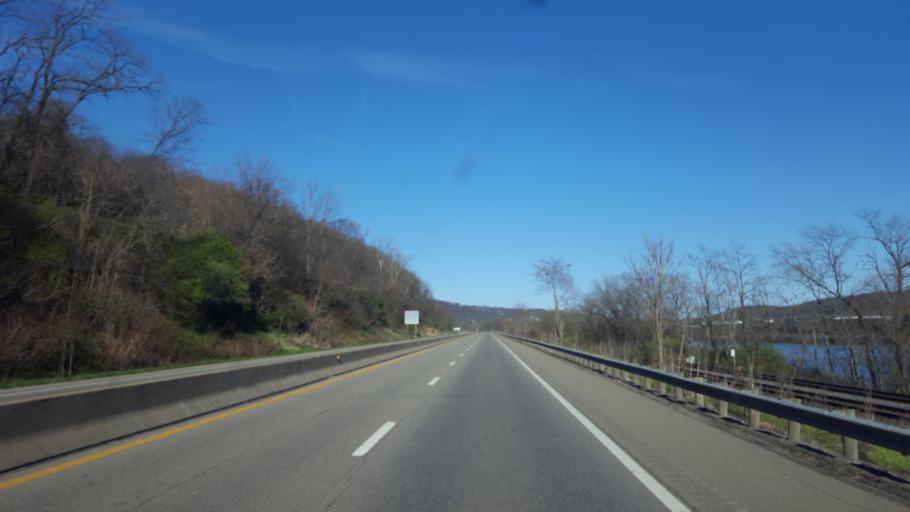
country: US
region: West Virginia
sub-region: Hancock County
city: Newell
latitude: 40.6210
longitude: -80.6243
